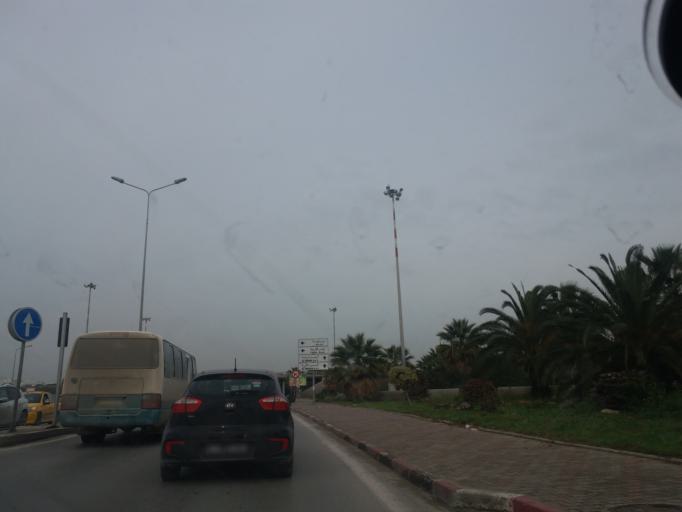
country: TN
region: Tunis
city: Tunis
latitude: 36.8395
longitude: 10.1709
